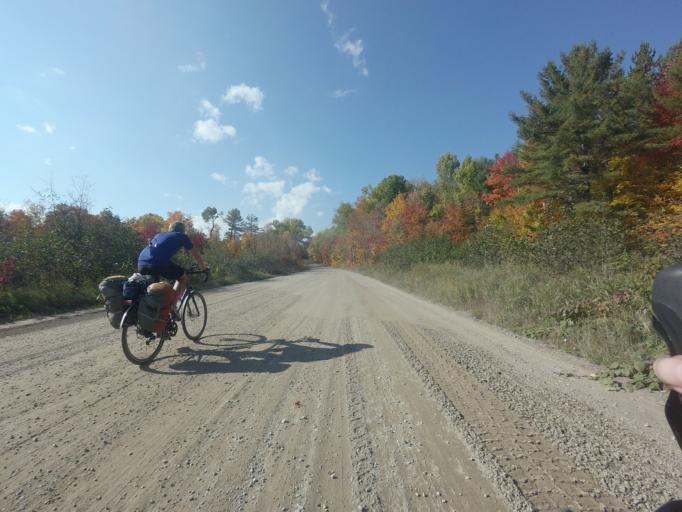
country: CA
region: Ontario
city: Petawawa
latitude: 45.8174
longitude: -77.4303
